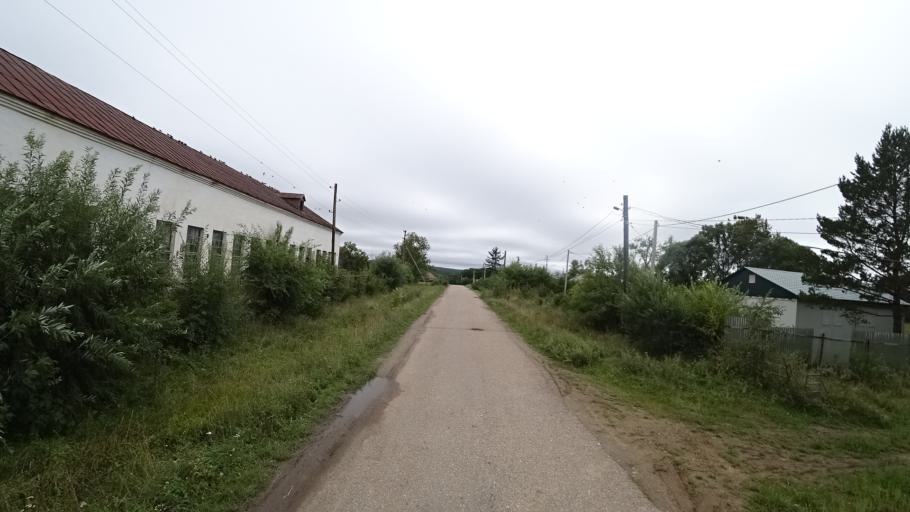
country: RU
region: Primorskiy
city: Monastyrishche
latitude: 44.0811
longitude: 132.5827
